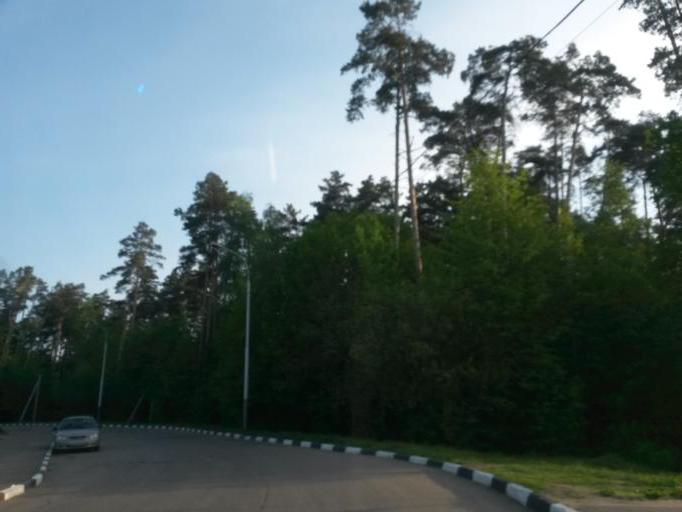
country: RU
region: Moskovskaya
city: Shcherbinka
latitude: 55.5038
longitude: 37.6221
